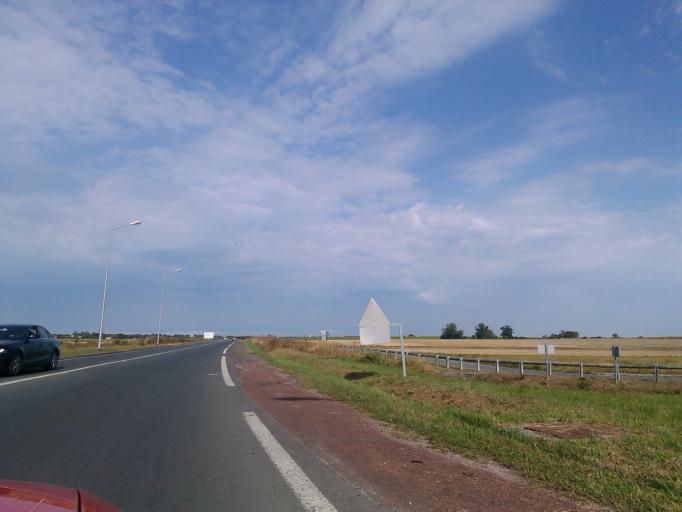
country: FR
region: Poitou-Charentes
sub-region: Departement de la Charente-Maritime
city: Etaules
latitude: 45.7417
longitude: -1.0926
